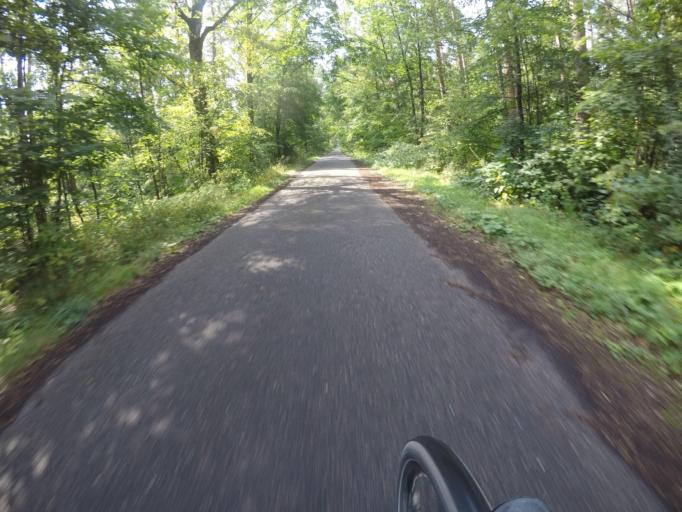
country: DE
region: Baden-Wuerttemberg
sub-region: Karlsruhe Region
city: Ketsch
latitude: 49.3603
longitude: 8.5560
